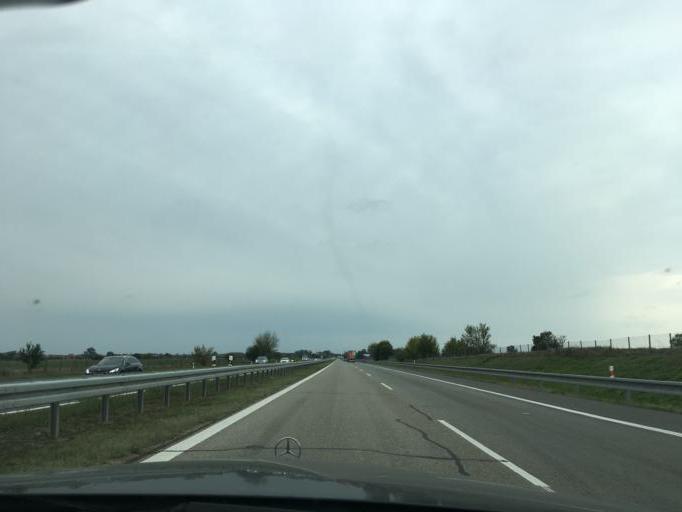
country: CZ
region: South Moravian
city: Kostice
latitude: 48.7561
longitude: 16.9528
